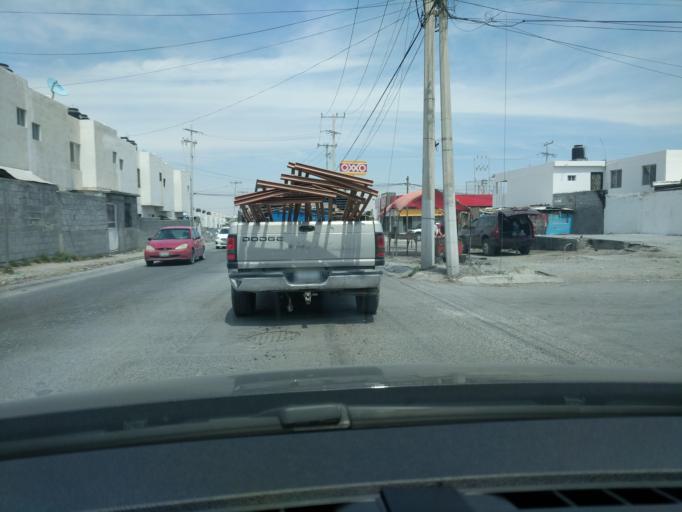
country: MX
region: Coahuila
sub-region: Arteaga
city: Arteaga
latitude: 25.4283
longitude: -100.9119
